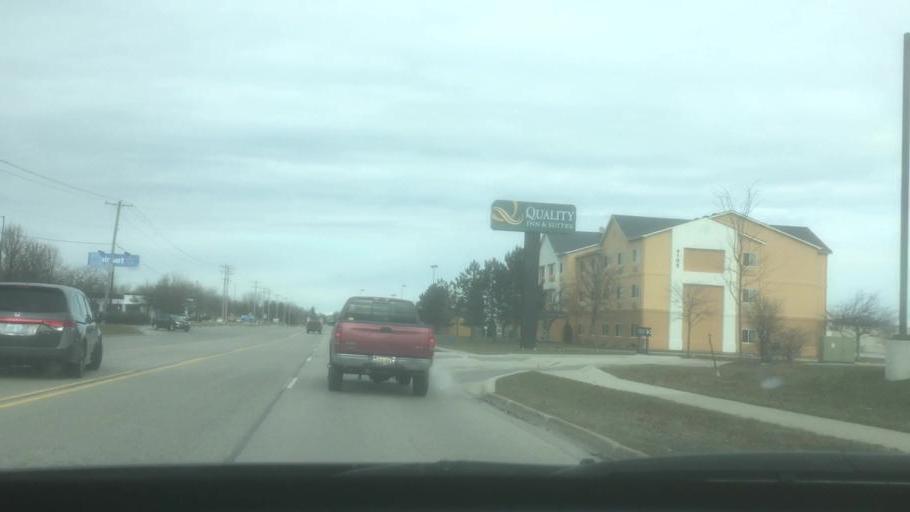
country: US
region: Michigan
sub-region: Bay County
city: Bay City
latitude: 43.6240
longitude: -83.8942
